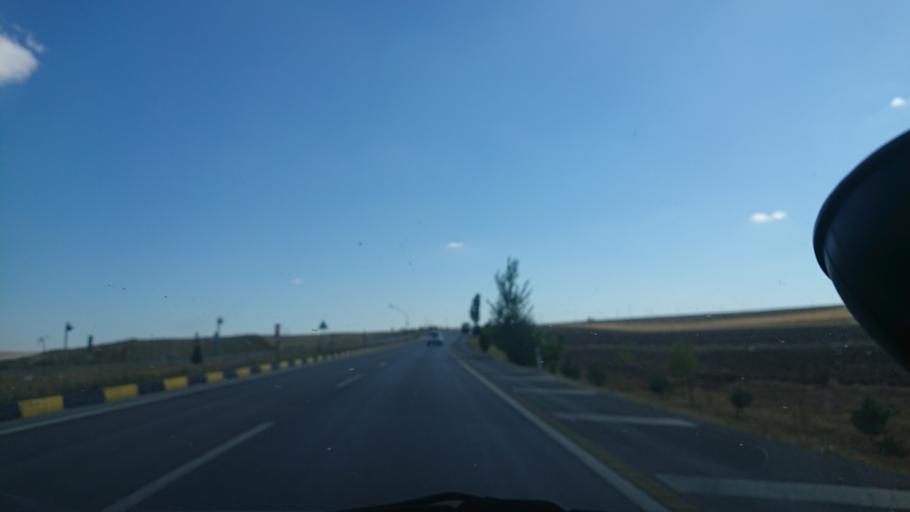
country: TR
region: Eskisehir
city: Mahmudiye
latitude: 39.5171
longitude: 30.9626
